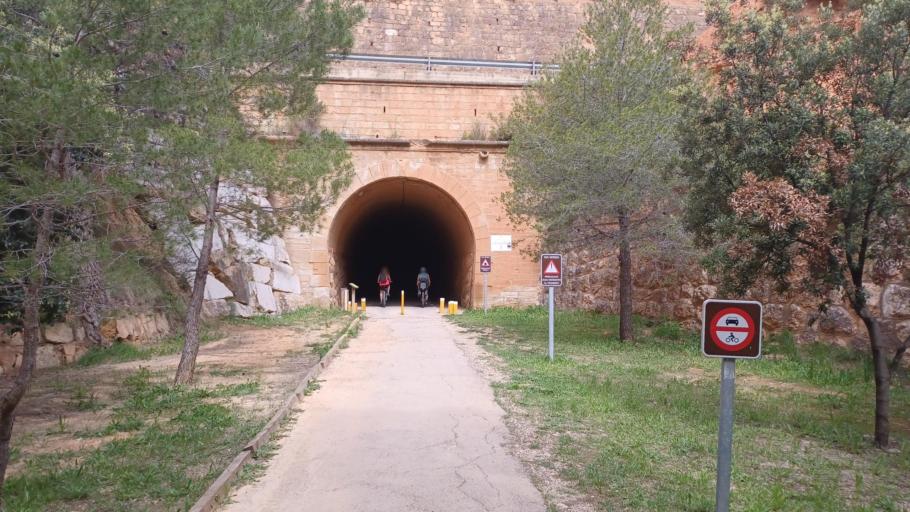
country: ES
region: Catalonia
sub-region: Provincia de Tarragona
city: Bot
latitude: 41.0036
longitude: 0.4185
